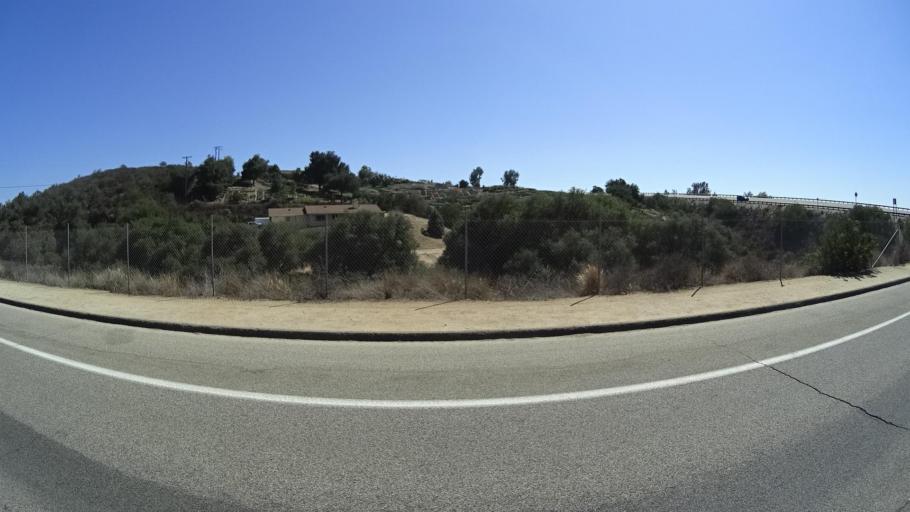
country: US
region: California
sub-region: San Diego County
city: Bonsall
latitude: 33.3010
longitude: -117.1526
